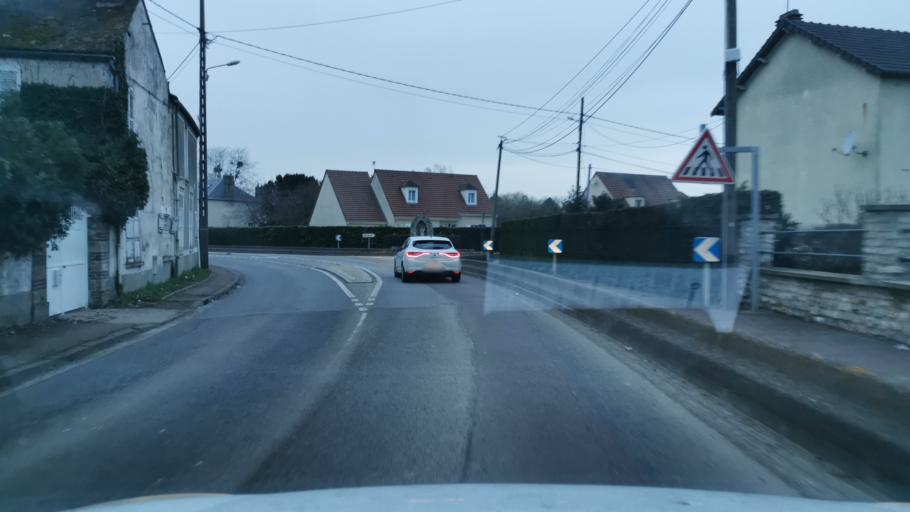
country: FR
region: Ile-de-France
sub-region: Departement des Yvelines
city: Longnes
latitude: 48.9228
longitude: 1.5899
